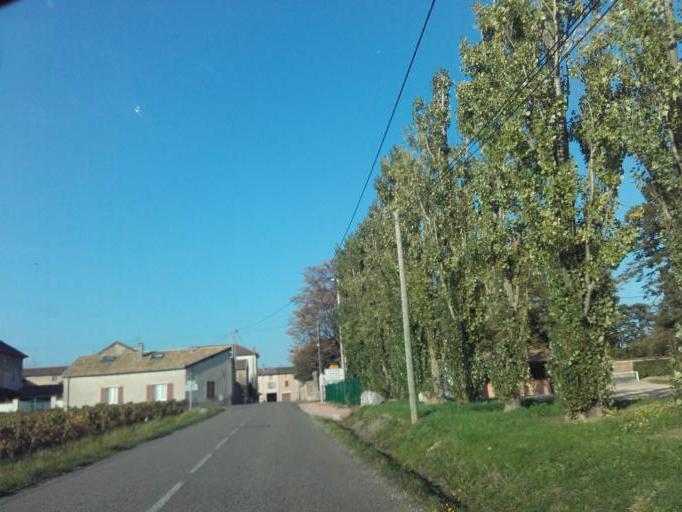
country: FR
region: Bourgogne
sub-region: Departement de Saone-et-Loire
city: La Chapelle-de-Guinchay
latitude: 46.2404
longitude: 4.7499
